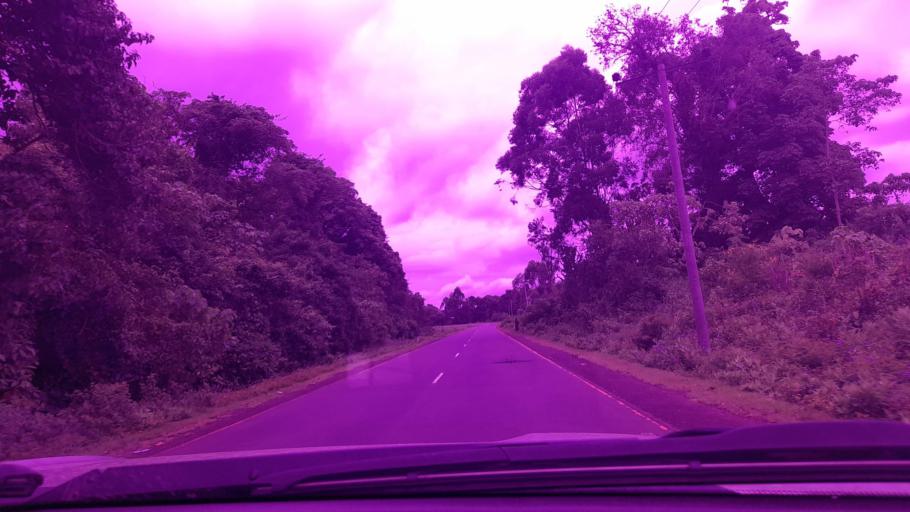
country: ET
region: Southern Nations, Nationalities, and People's Region
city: Bonga
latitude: 7.2825
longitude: 35.9590
